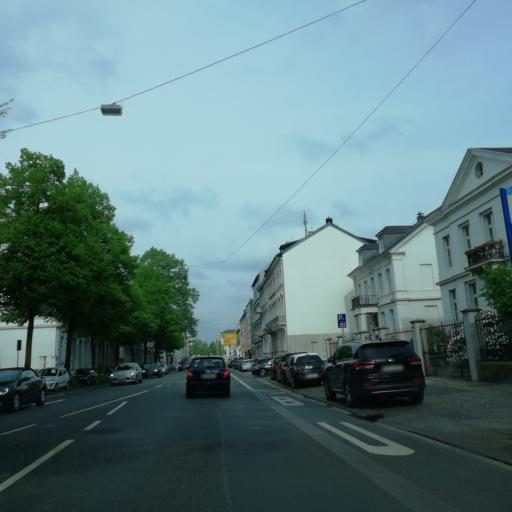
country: DE
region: North Rhine-Westphalia
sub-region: Regierungsbezirk Dusseldorf
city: Wuppertal
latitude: 51.2515
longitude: 7.1292
